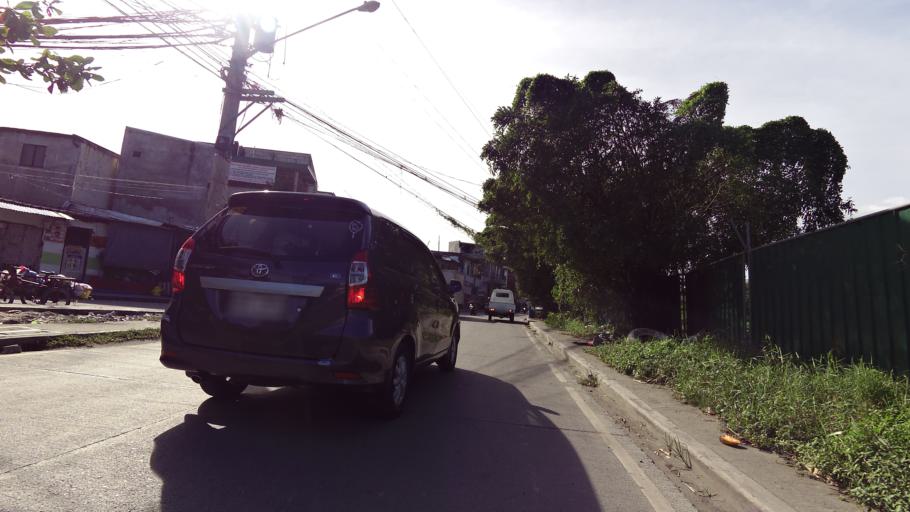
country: PH
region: Calabarzon
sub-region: Province of Rizal
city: Taytay
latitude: 14.5422
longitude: 121.1105
